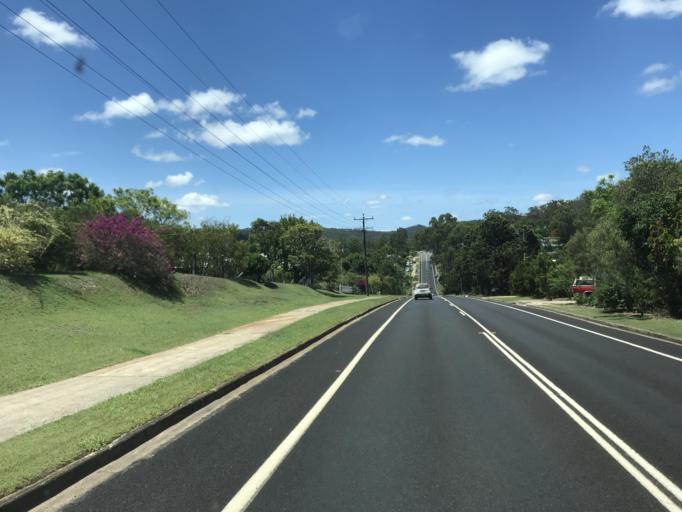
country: AU
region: Queensland
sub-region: Tablelands
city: Atherton
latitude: -17.3909
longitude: 145.3873
